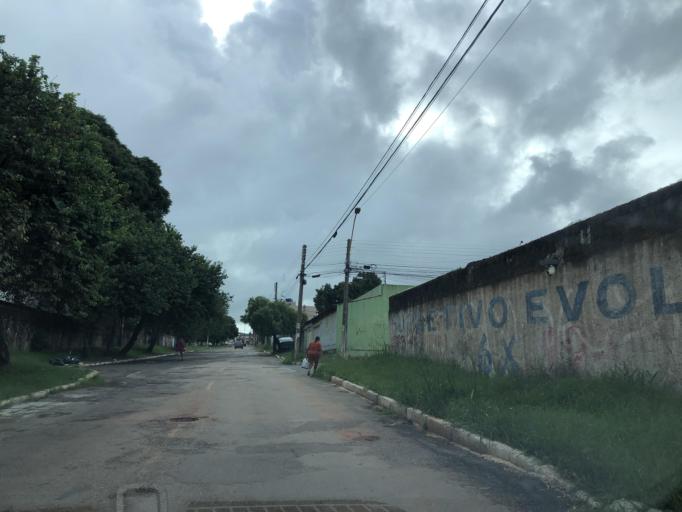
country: BR
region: Federal District
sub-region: Brasilia
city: Brasilia
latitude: -15.8330
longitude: -48.0915
